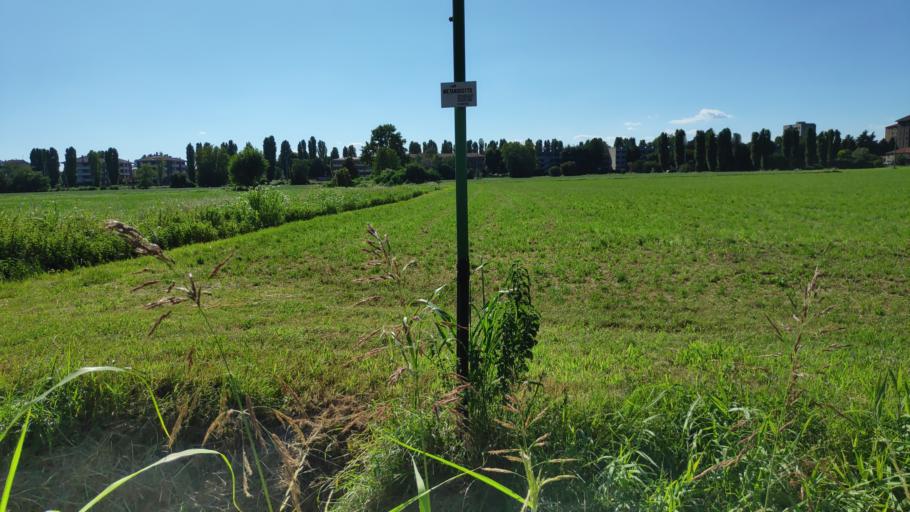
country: IT
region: Lombardy
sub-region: Citta metropolitana di Milano
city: Melzo
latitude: 45.4988
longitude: 9.4378
